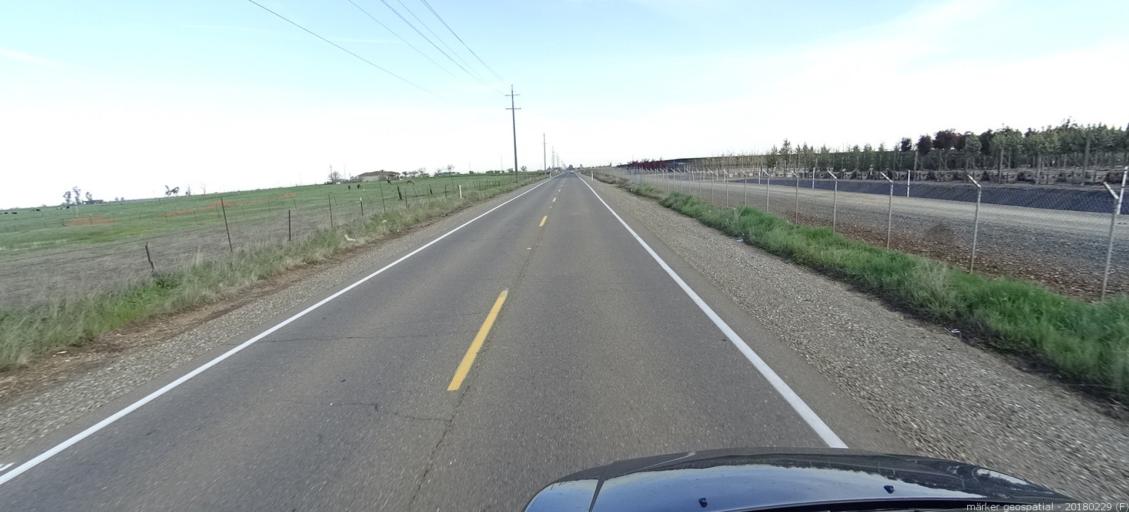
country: US
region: California
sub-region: Sacramento County
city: Vineyard
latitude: 38.4908
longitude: -121.2977
